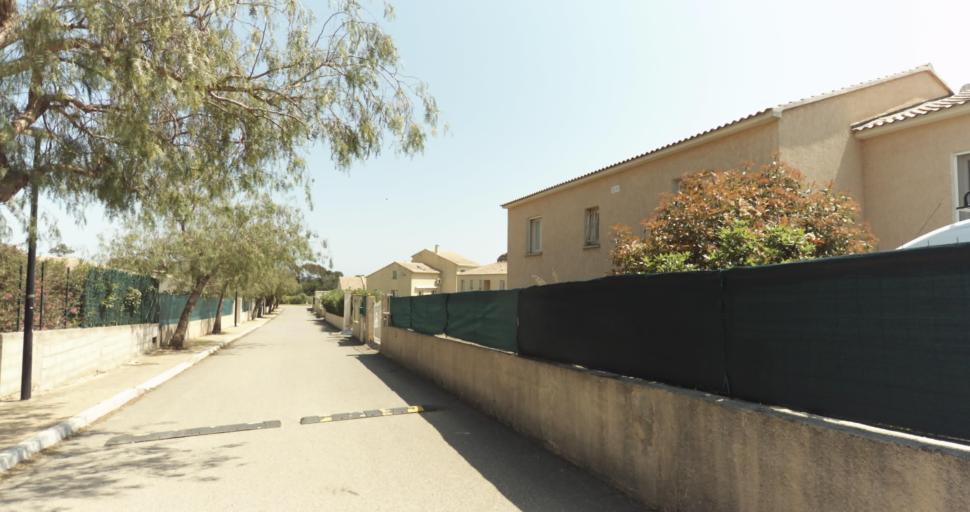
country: FR
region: Corsica
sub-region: Departement de la Haute-Corse
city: Biguglia
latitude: 42.6006
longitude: 9.4326
